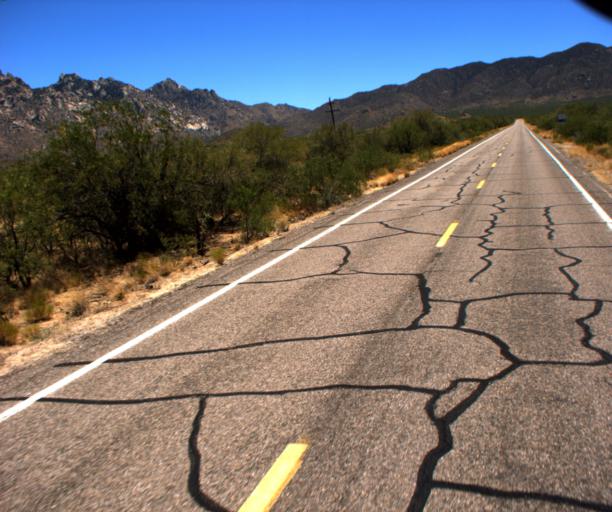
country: US
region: Arizona
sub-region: Pima County
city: Three Points
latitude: 32.0182
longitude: -111.5759
